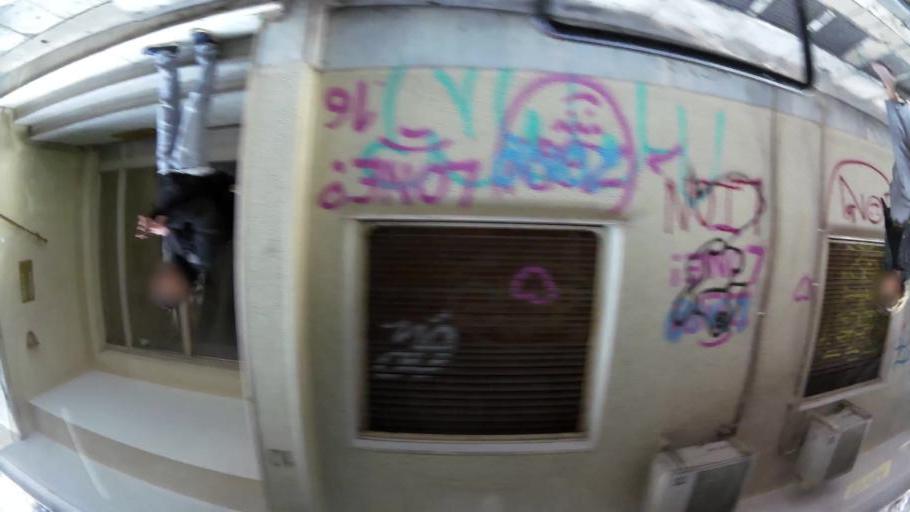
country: GR
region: Attica
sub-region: Nomarchia Athinas
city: Athens
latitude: 37.9736
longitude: 23.7309
